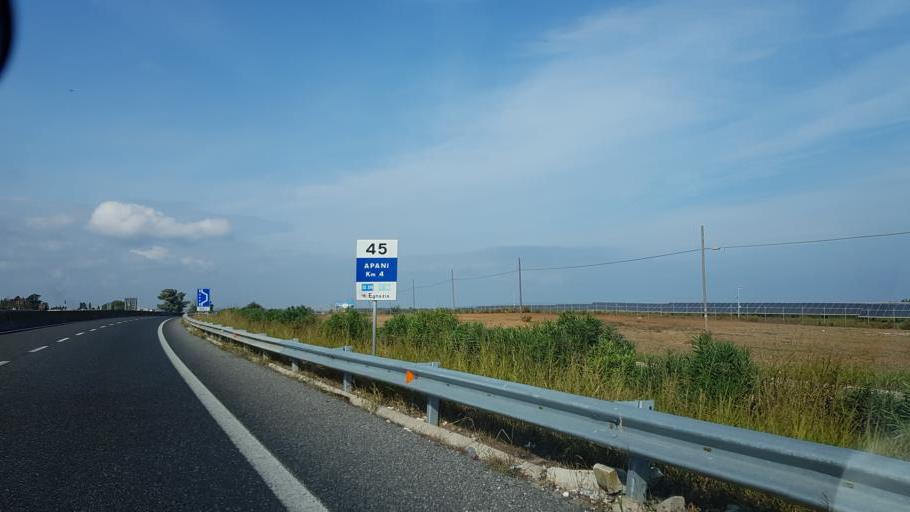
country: IT
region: Apulia
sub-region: Provincia di Brindisi
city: Brindisi
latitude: 40.6702
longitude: 17.8586
